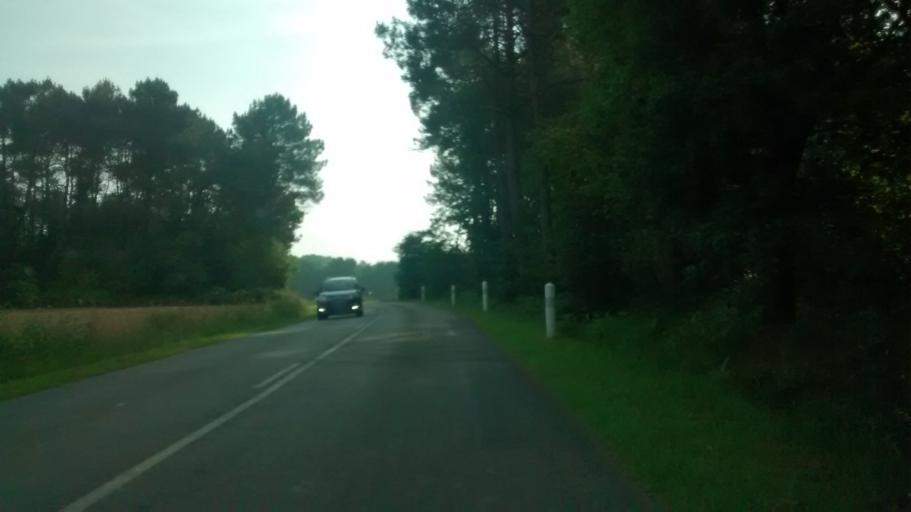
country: FR
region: Brittany
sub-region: Departement du Morbihan
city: Ruffiac
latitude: 47.8545
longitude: -2.2456
